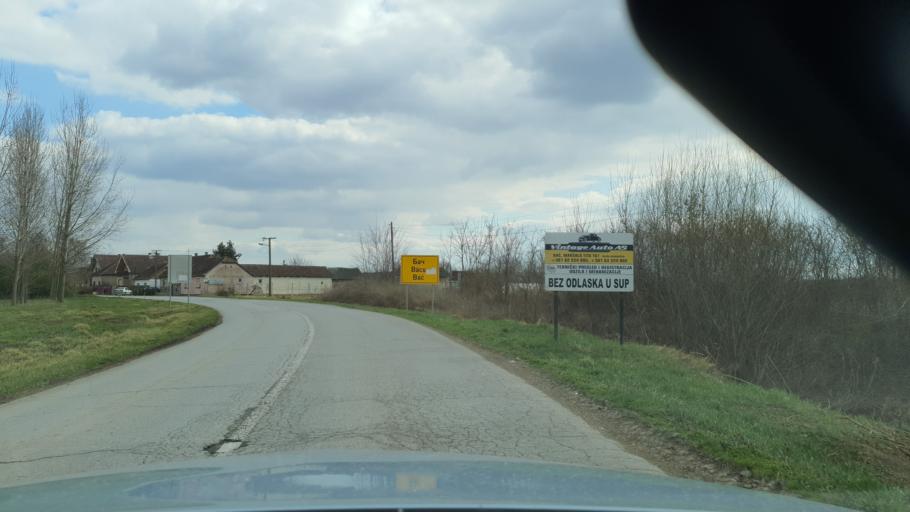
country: RS
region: Autonomna Pokrajina Vojvodina
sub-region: Juznobacki Okrug
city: Bac
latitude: 45.3891
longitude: 19.2206
